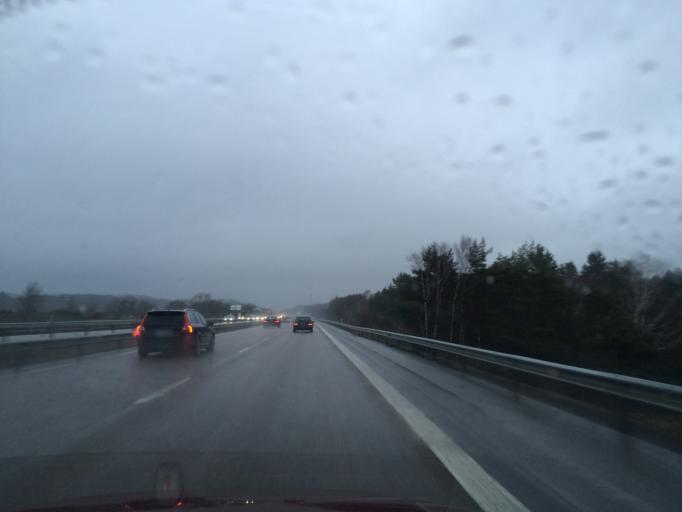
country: SE
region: Vaestra Goetaland
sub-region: Molndal
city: Lindome
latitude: 57.5377
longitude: 12.0514
